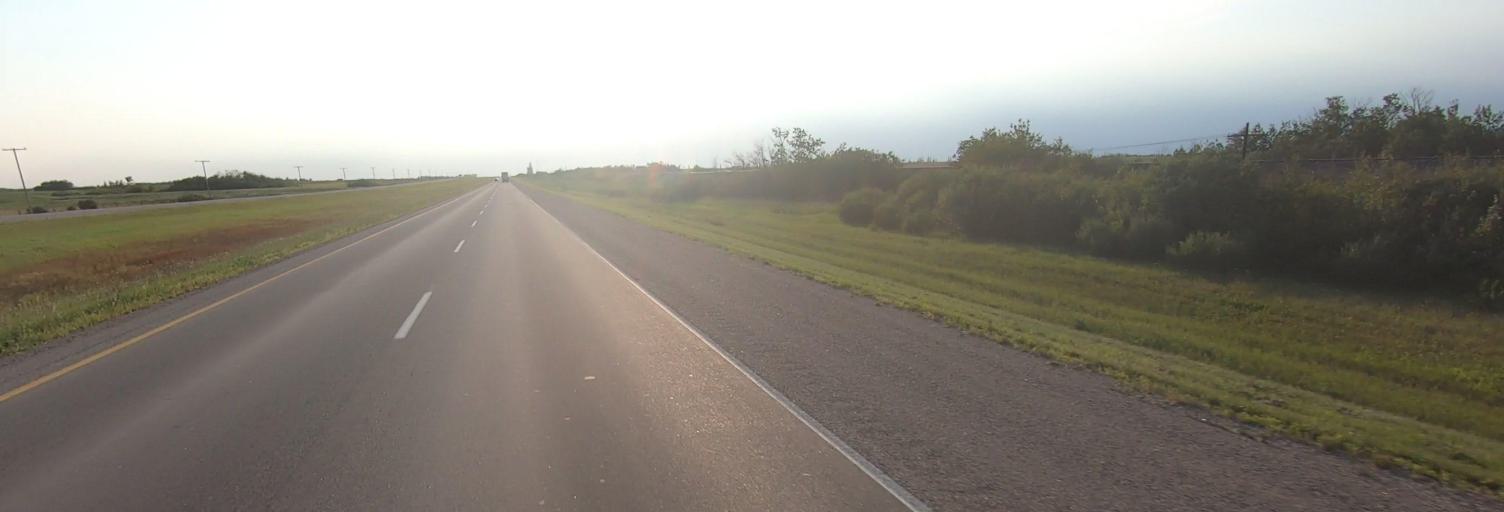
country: CA
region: Saskatchewan
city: White City
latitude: 50.5078
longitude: -104.1392
